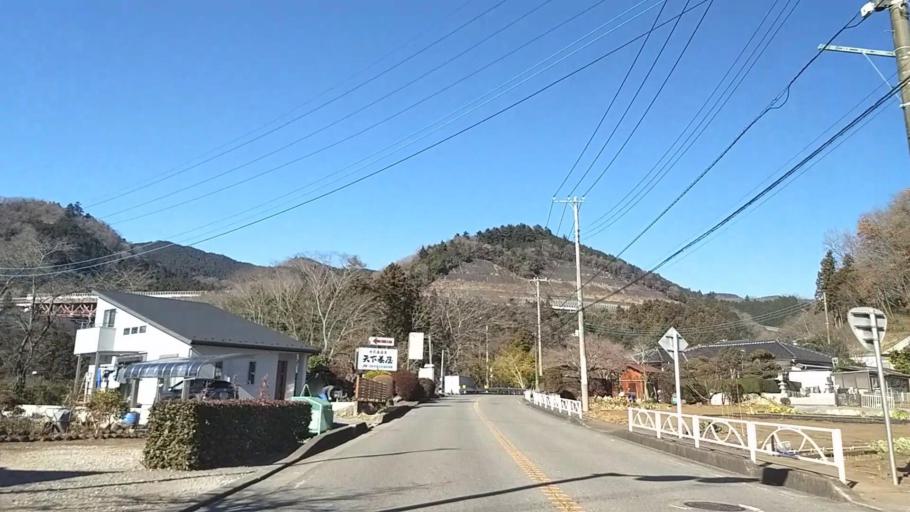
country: JP
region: Yamanashi
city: Uenohara
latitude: 35.6217
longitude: 139.2045
